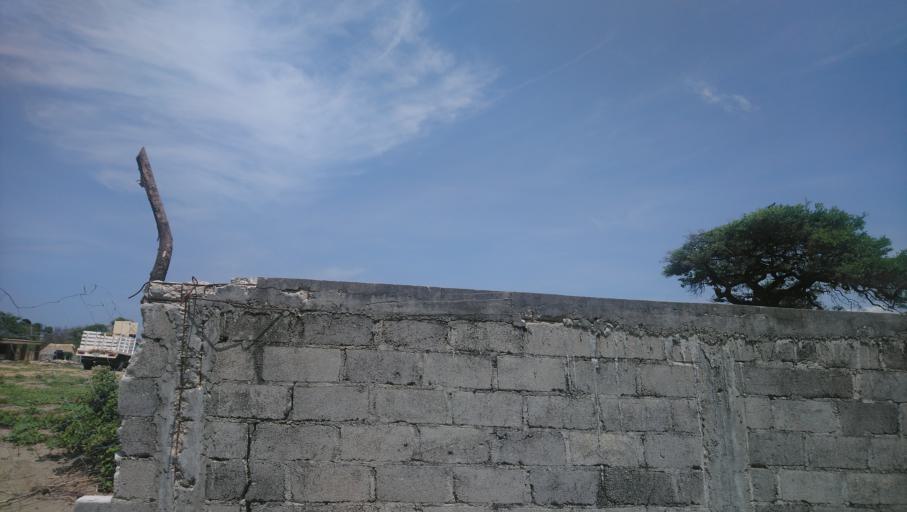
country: MX
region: Oaxaca
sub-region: Salina Cruz
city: Salina Cruz
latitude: 16.1913
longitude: -95.1199
